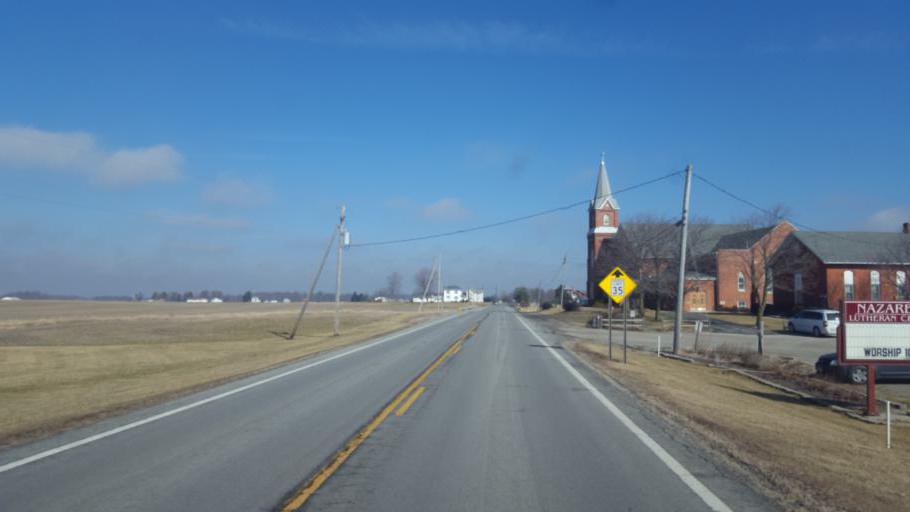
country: US
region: Ohio
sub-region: Crawford County
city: Bucyrus
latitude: 40.9426
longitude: -82.9468
